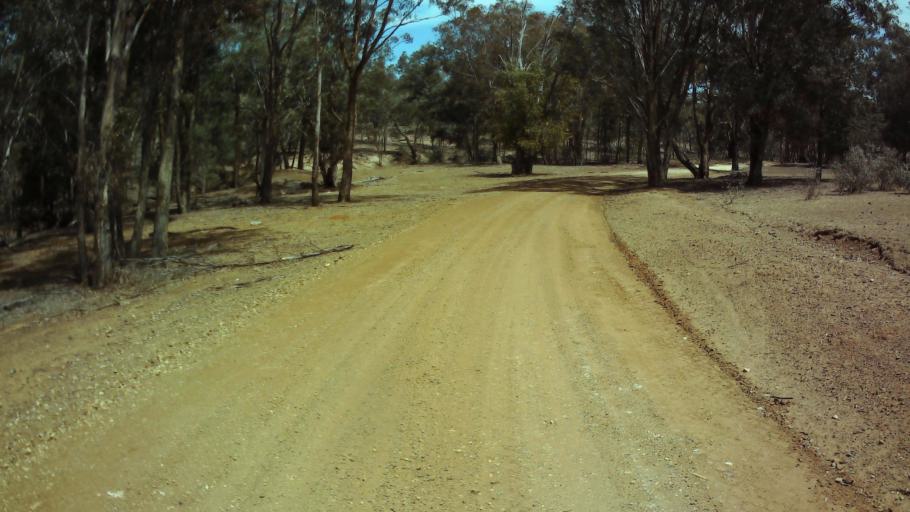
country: AU
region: New South Wales
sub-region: Weddin
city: Grenfell
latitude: -33.7979
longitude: 148.1603
